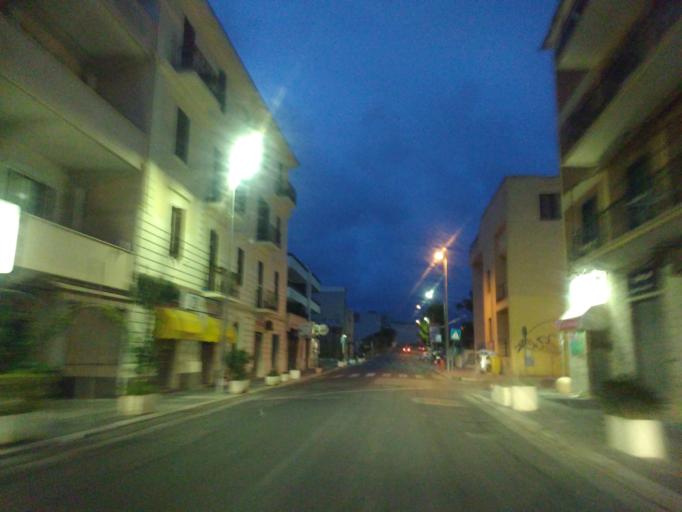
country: IT
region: Latium
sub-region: Citta metropolitana di Roma Capitale
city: Anzio
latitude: 41.4516
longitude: 12.6243
